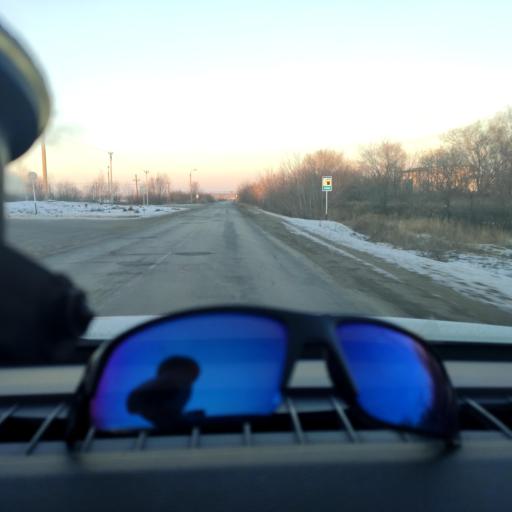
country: RU
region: Samara
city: Chapayevsk
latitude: 53.0055
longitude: 49.7436
